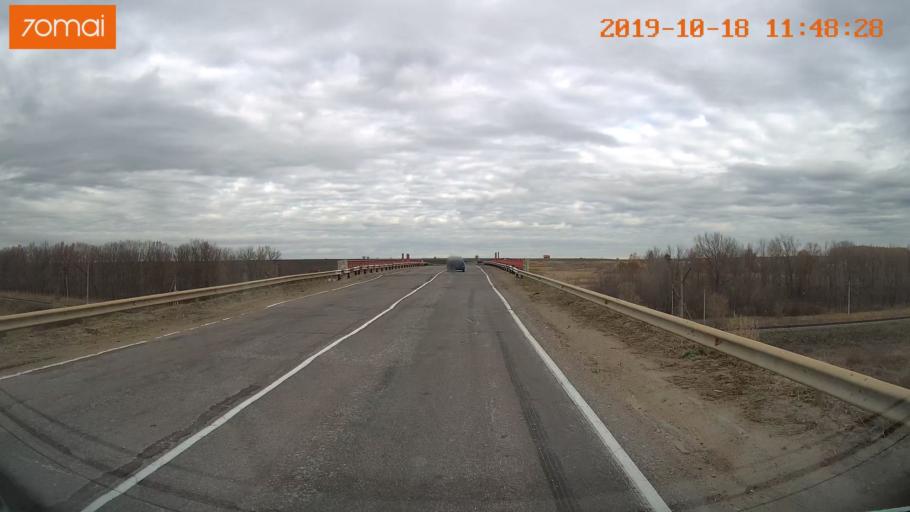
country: RU
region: Rjazan
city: Mikhaylov
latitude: 54.2398
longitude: 38.9828
